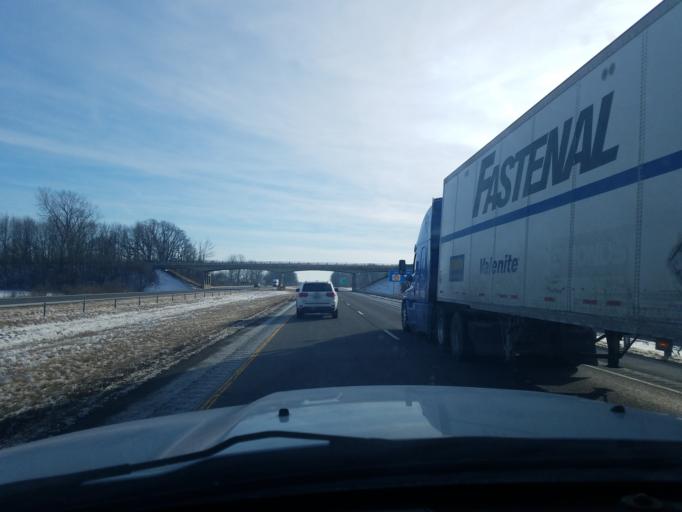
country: US
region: Indiana
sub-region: Madison County
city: Alexandria
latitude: 40.2928
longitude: -85.5584
